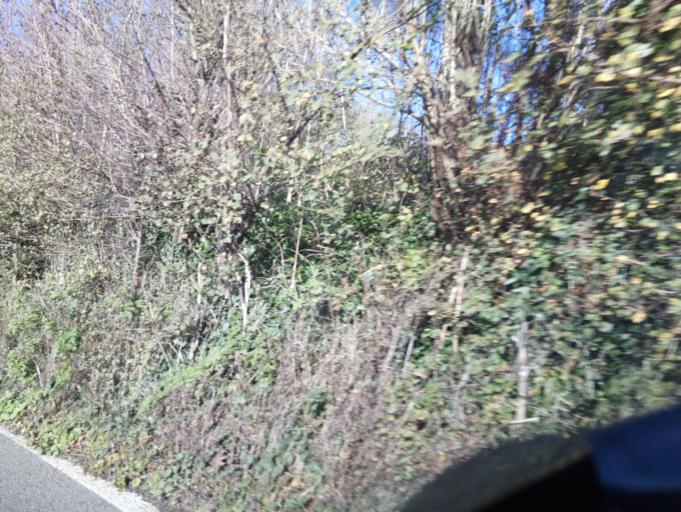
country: GB
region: England
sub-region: Somerset
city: Langport
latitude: 51.0507
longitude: -2.8296
